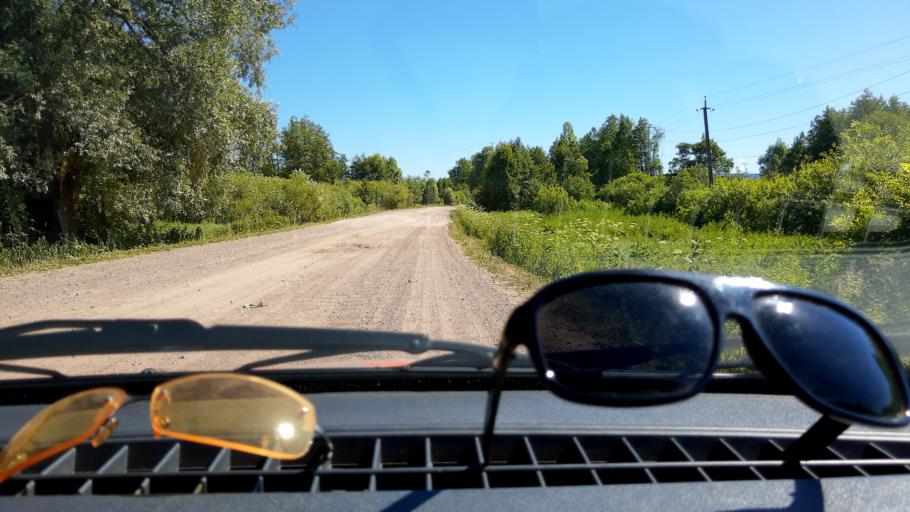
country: RU
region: Bashkortostan
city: Ulu-Telyak
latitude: 54.7731
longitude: 56.9829
